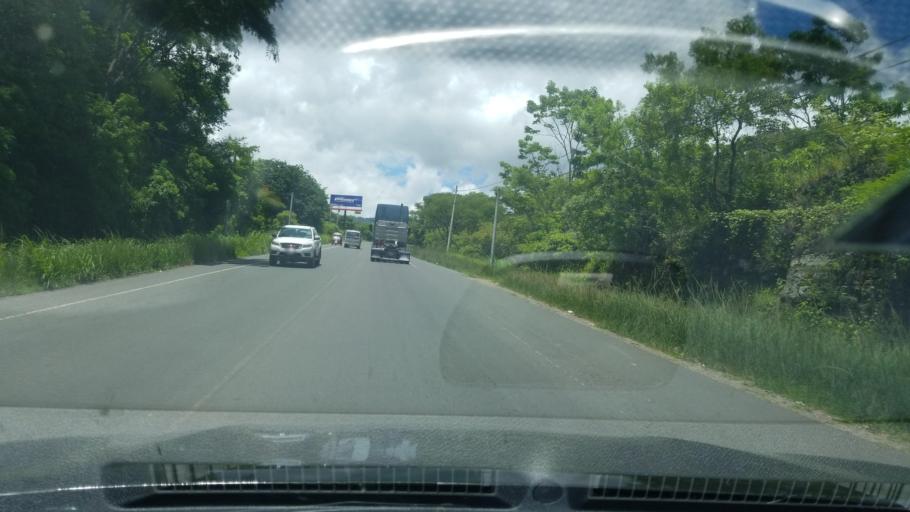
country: HN
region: Francisco Morazan
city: Rio Abajo
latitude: 14.1665
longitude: -87.2048
